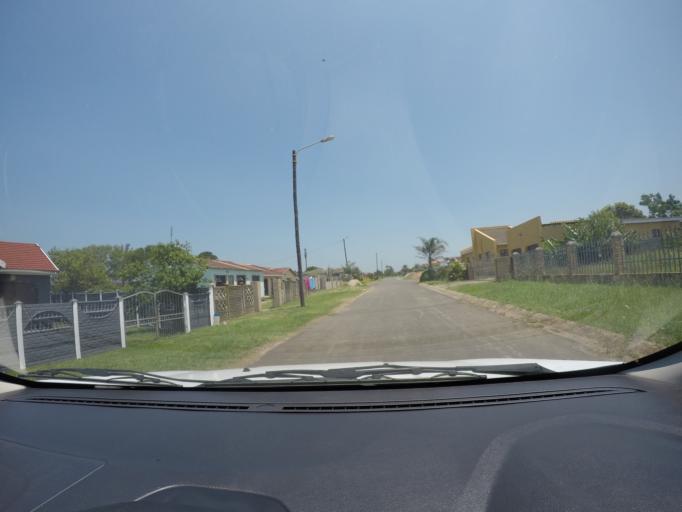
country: ZA
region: KwaZulu-Natal
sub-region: uThungulu District Municipality
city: eSikhawini
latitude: -28.8883
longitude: 31.8854
